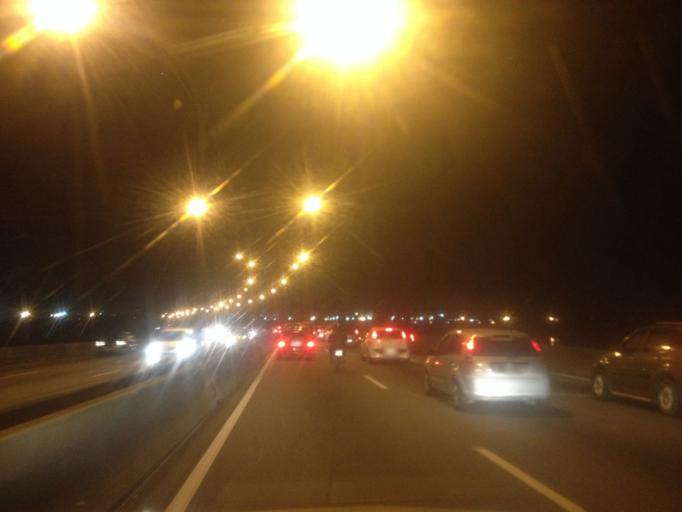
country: BR
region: Rio de Janeiro
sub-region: Duque De Caxias
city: Duque de Caxias
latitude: -22.8119
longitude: -43.2703
